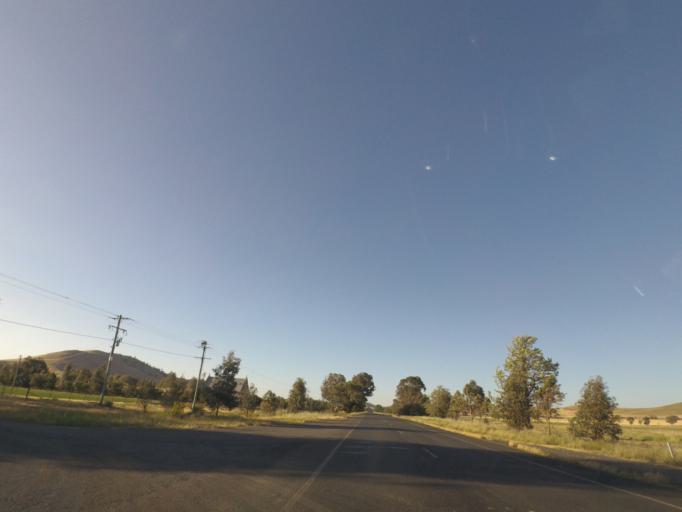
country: AU
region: New South Wales
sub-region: Gundagai
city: Gundagai
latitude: -34.9441
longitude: 148.1687
